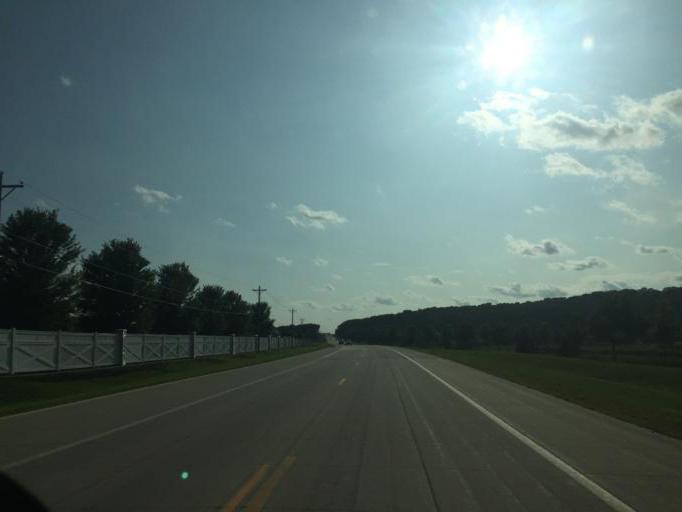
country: US
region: Minnesota
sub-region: Olmsted County
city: Rochester
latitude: 44.0032
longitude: -92.5176
